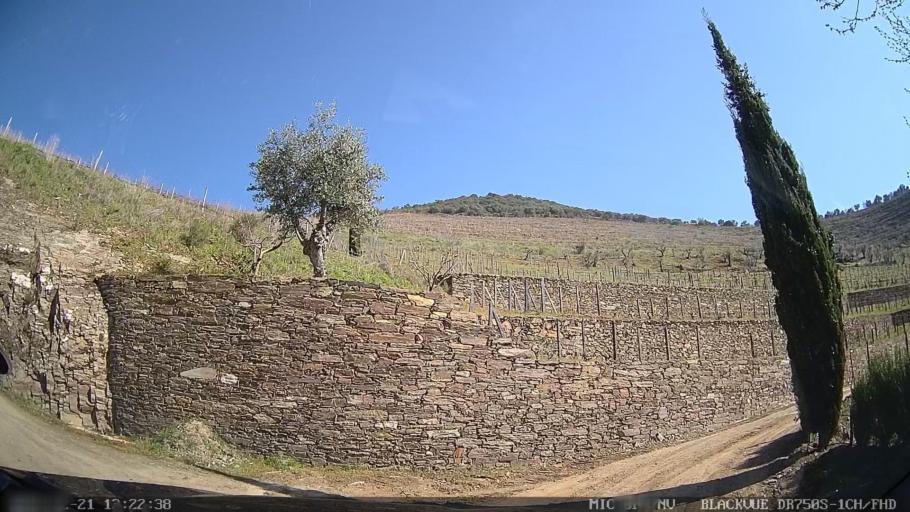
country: PT
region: Viseu
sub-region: Tabuaco
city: Tabuaco
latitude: 41.1761
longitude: -7.5460
